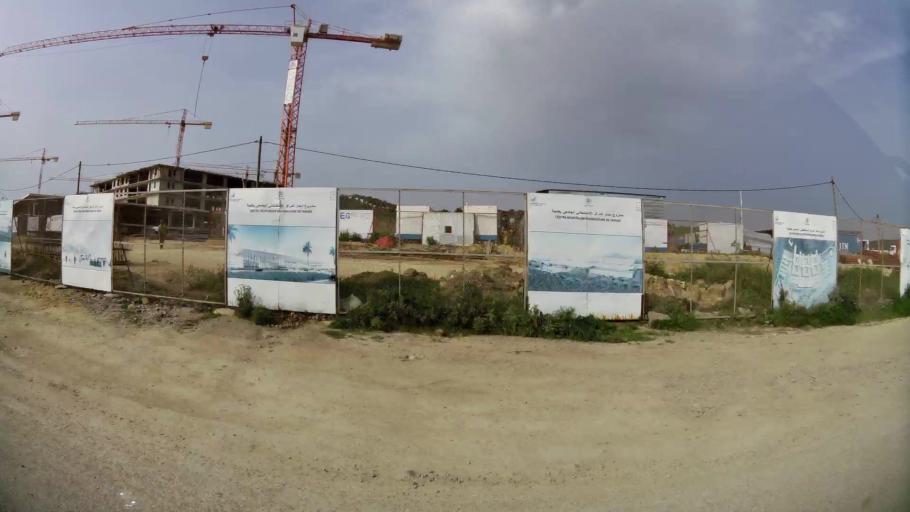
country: MA
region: Tanger-Tetouan
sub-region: Tanger-Assilah
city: Boukhalef
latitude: 35.6826
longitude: -5.9265
